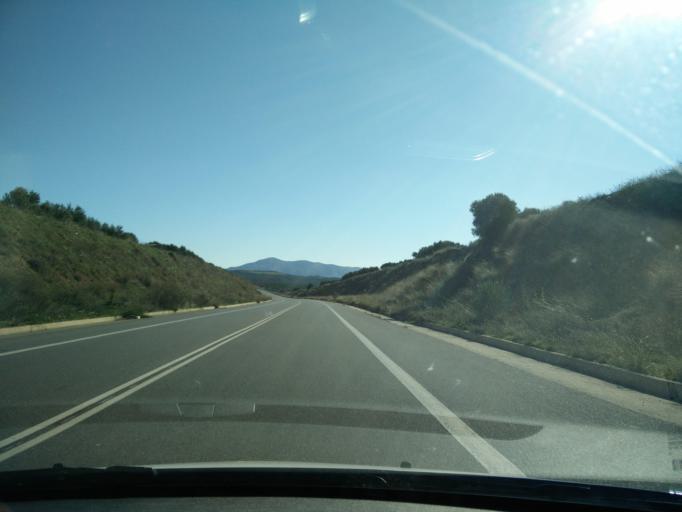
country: GR
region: Crete
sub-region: Nomos Irakleiou
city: Arkalochori
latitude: 35.1098
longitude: 25.2910
